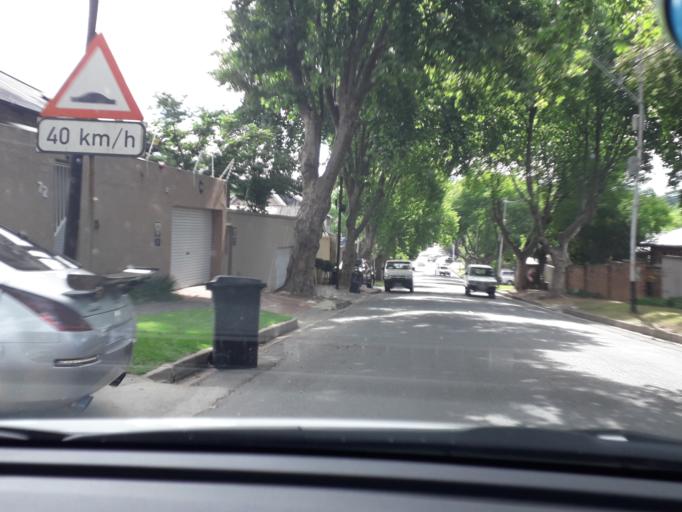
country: ZA
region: Gauteng
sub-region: City of Johannesburg Metropolitan Municipality
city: Johannesburg
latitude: -26.1556
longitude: 28.0721
